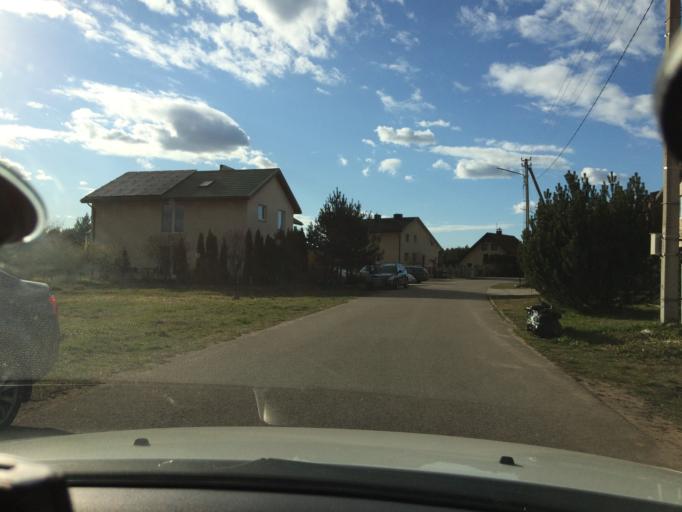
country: LT
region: Vilnius County
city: Rasos
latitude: 54.7761
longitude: 25.3486
